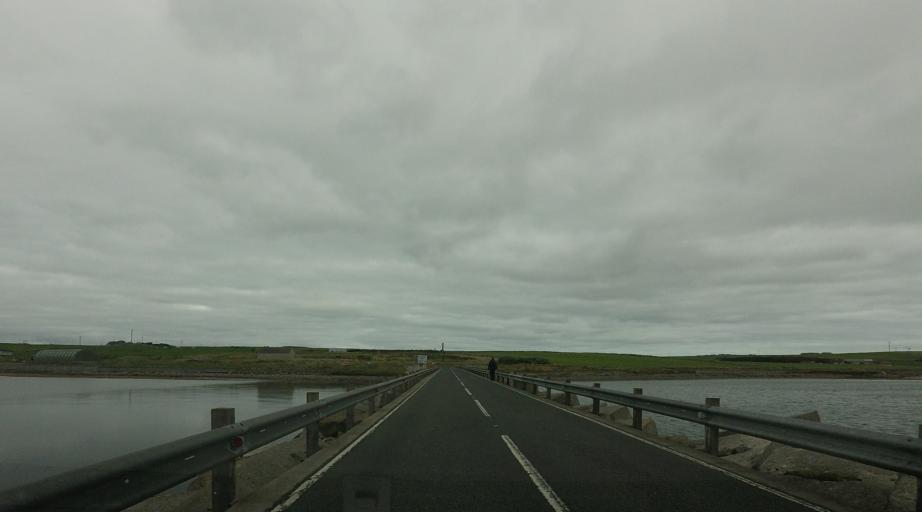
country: GB
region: Scotland
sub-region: Orkney Islands
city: Kirkwall
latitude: 58.8942
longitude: -2.8968
